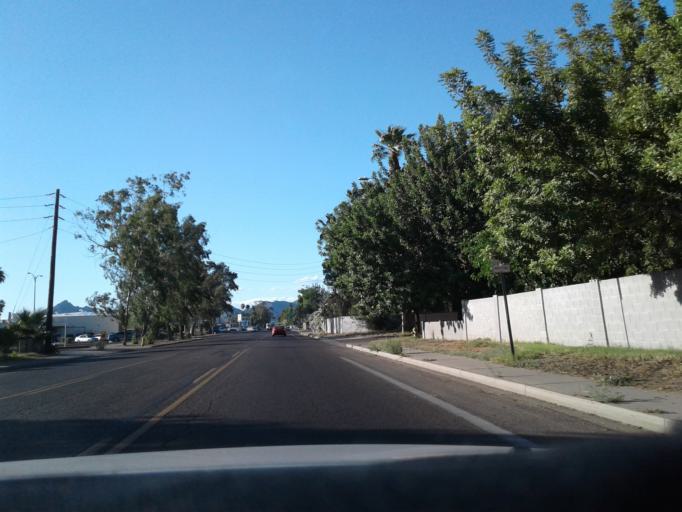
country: US
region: Arizona
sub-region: Maricopa County
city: Paradise Valley
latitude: 33.4776
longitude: -111.9955
